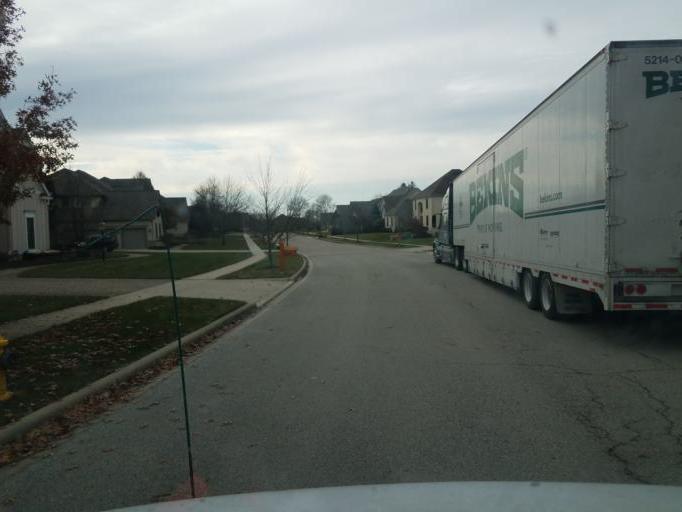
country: US
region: Ohio
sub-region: Franklin County
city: Westerville
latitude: 40.1800
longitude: -82.9365
